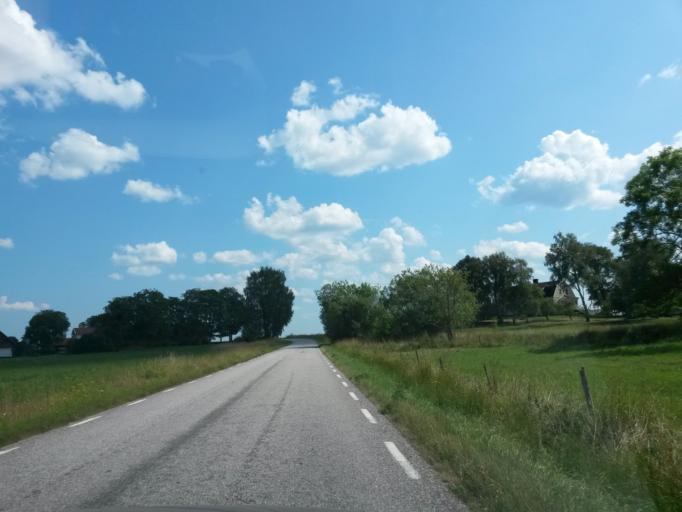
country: SE
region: Vaestra Goetaland
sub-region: Herrljunga Kommun
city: Herrljunga
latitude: 58.0857
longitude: 12.9739
